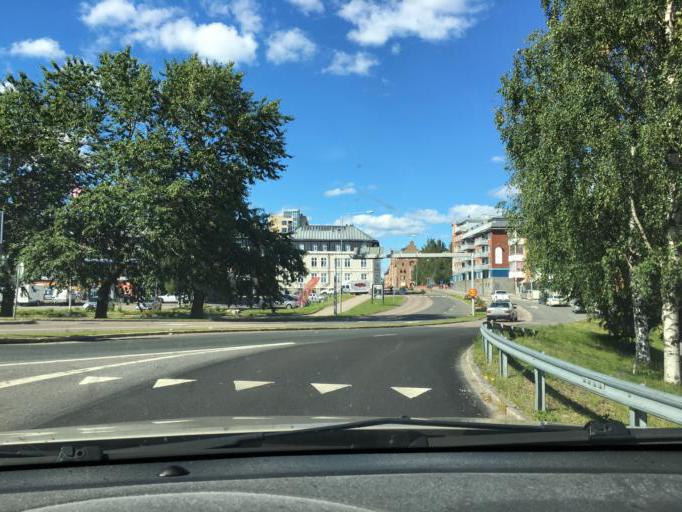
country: SE
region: Norrbotten
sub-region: Lulea Kommun
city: Lulea
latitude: 65.5809
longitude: 22.1457
